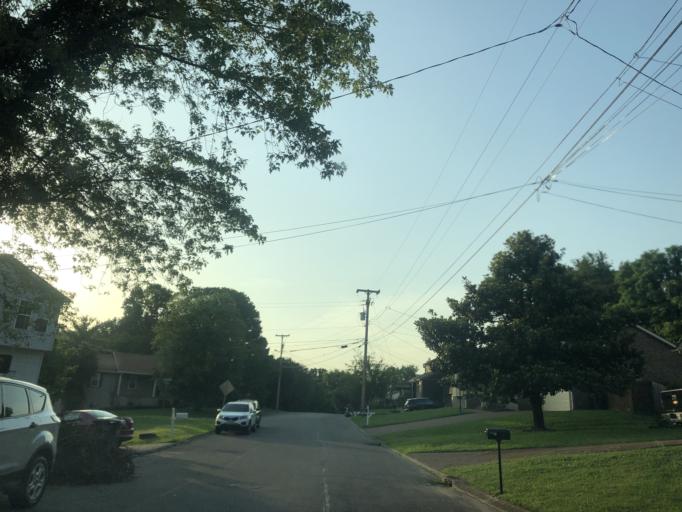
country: US
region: Tennessee
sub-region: Davidson County
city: Lakewood
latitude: 36.1357
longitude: -86.6339
